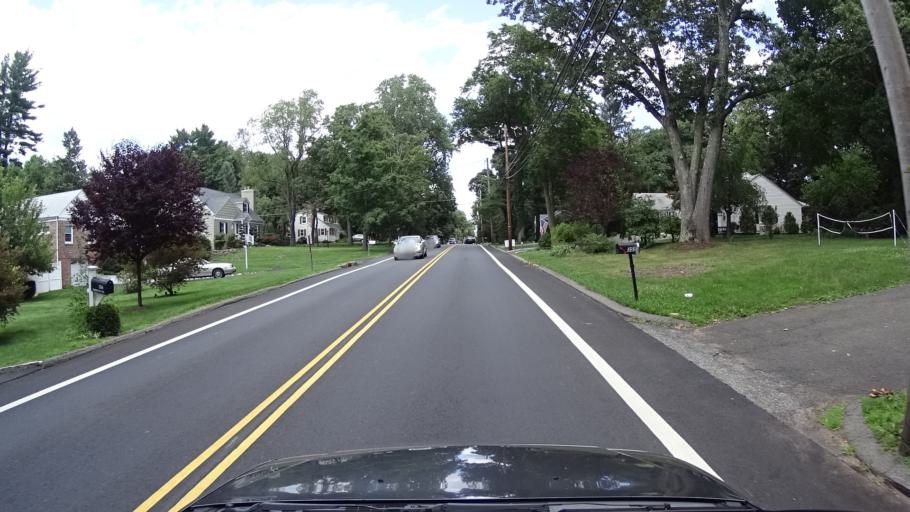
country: US
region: New Jersey
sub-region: Union County
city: New Providence
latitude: 40.7229
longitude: -74.4017
